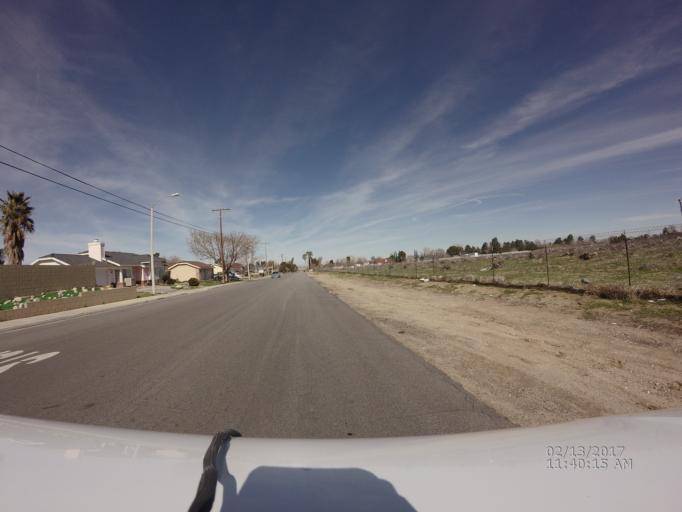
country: US
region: California
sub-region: Los Angeles County
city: Littlerock
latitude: 34.5232
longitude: -117.9969
